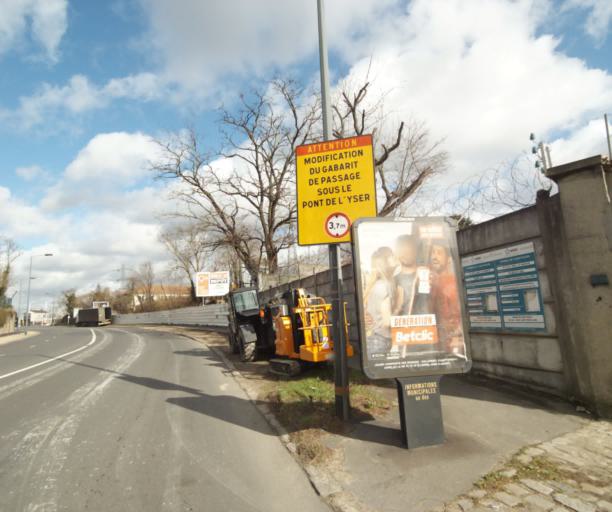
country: FR
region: Ile-de-France
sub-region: Departement de Seine-Saint-Denis
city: Villetaneuse
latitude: 48.9455
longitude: 2.3429
